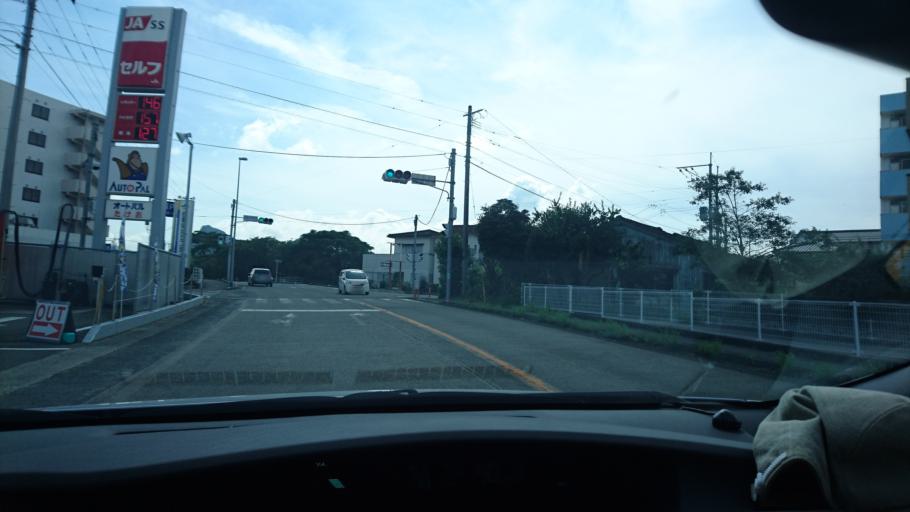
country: JP
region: Saga Prefecture
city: Takeocho-takeo
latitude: 33.2022
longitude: 130.0298
